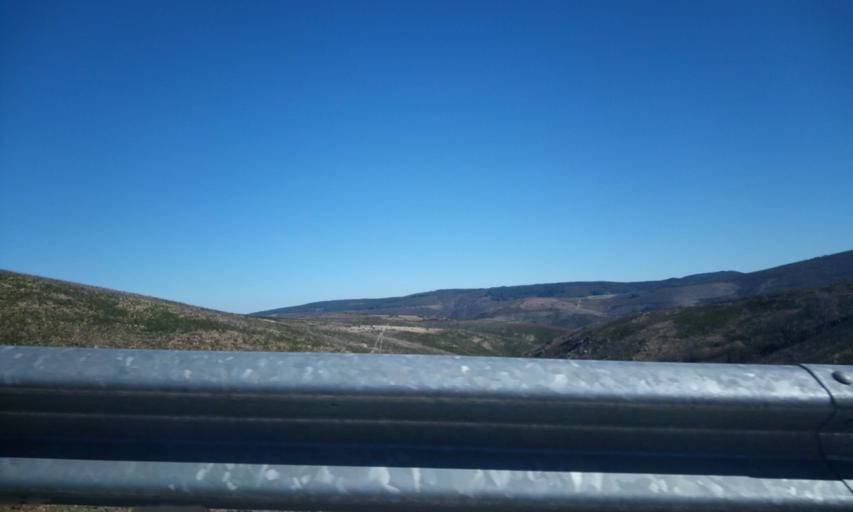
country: PT
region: Guarda
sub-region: Manteigas
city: Manteigas
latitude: 40.4685
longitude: -7.5198
